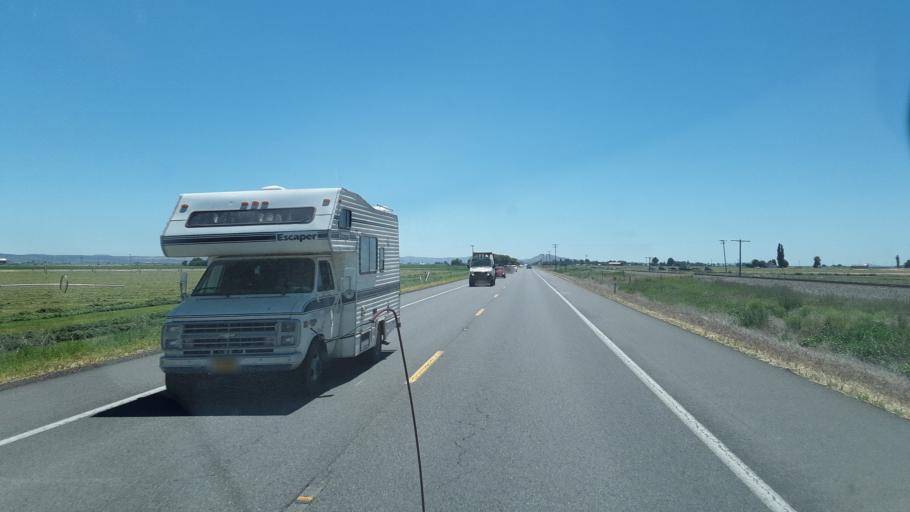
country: US
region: California
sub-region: Siskiyou County
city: Tulelake
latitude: 41.9815
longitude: -121.5010
